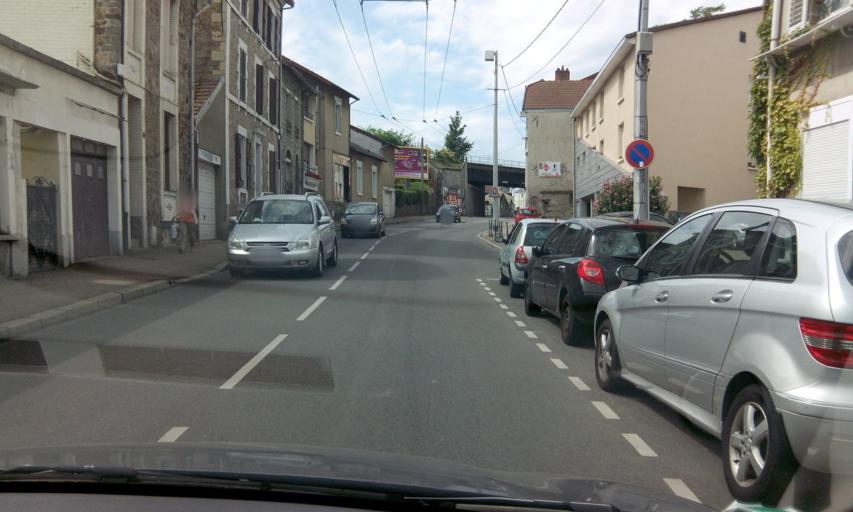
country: FR
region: Limousin
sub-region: Departement de la Haute-Vienne
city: Limoges
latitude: 45.8424
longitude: 1.2719
